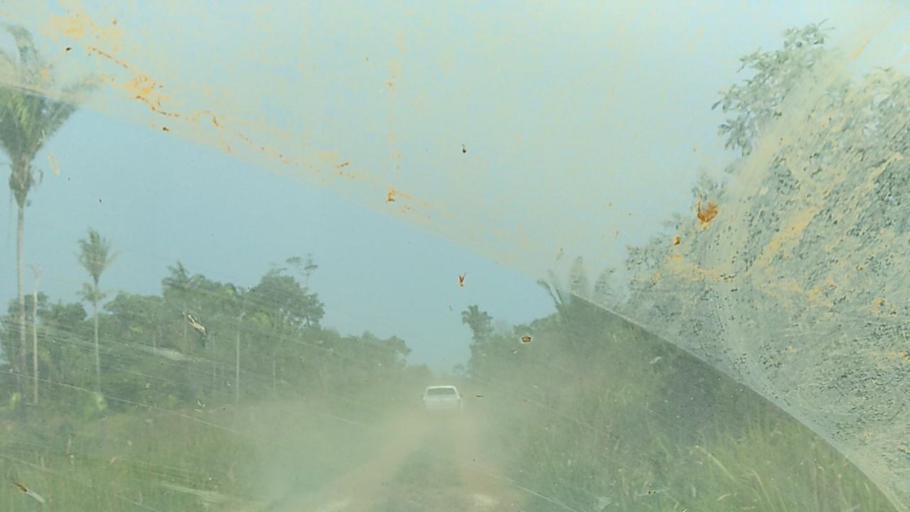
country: BR
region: Rondonia
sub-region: Porto Velho
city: Porto Velho
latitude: -8.9674
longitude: -64.3918
